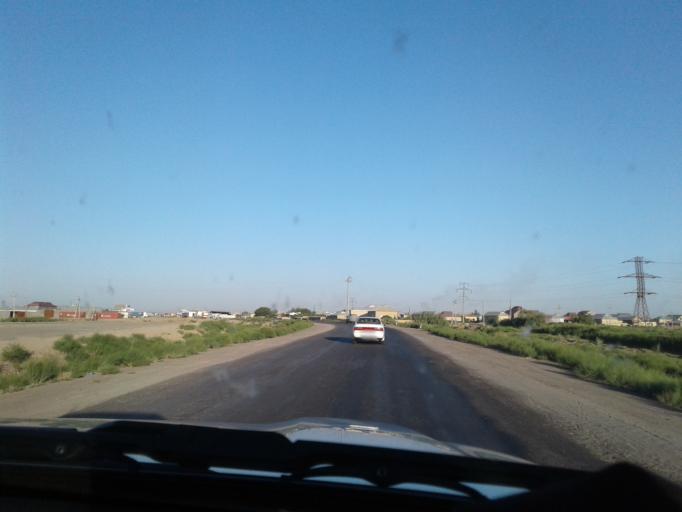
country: TM
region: Mary
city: Mary
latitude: 37.5676
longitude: 61.8101
